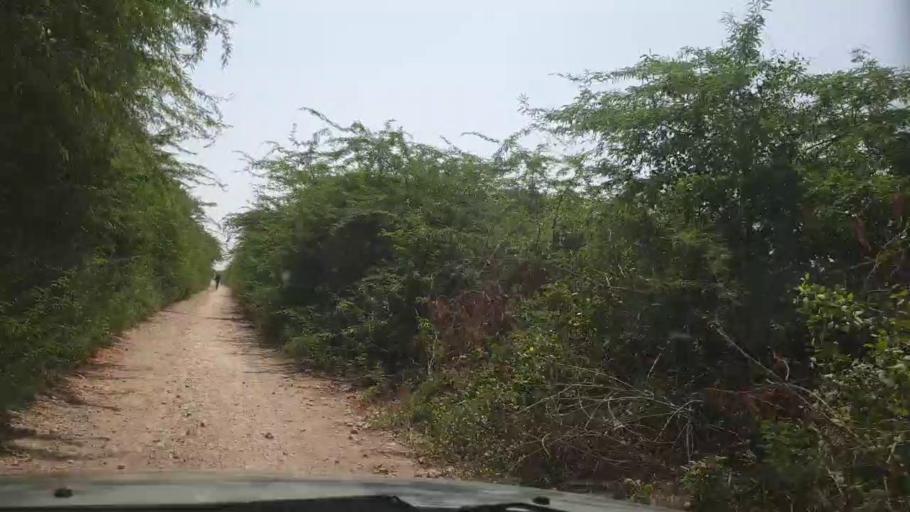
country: PK
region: Sindh
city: Tando Ghulam Ali
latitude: 25.1126
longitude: 68.8101
